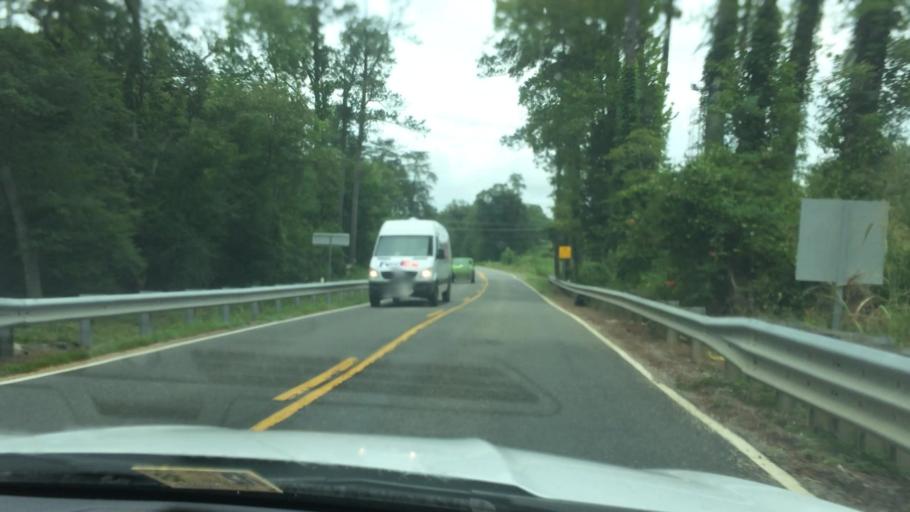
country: US
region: Virginia
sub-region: Charles City County
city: Charles City
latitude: 37.4324
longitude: -77.0374
